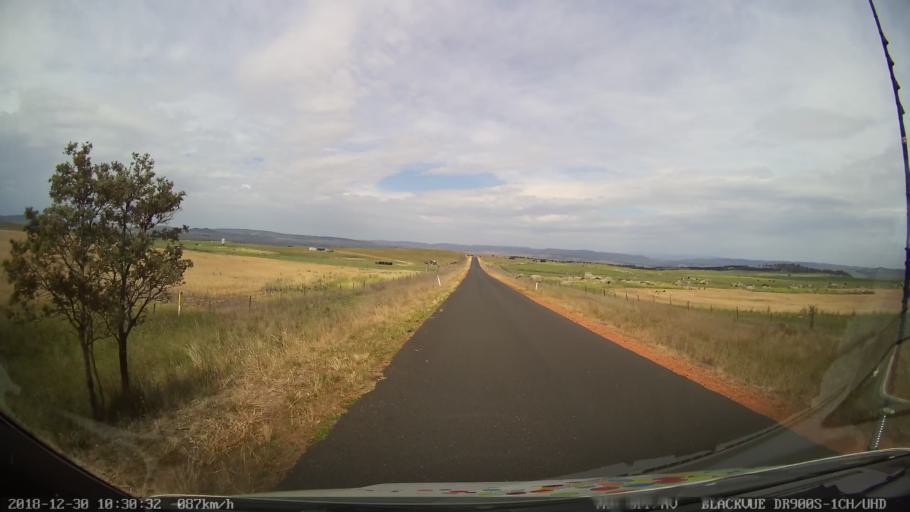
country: AU
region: New South Wales
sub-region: Snowy River
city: Berridale
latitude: -36.5040
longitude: 148.8937
